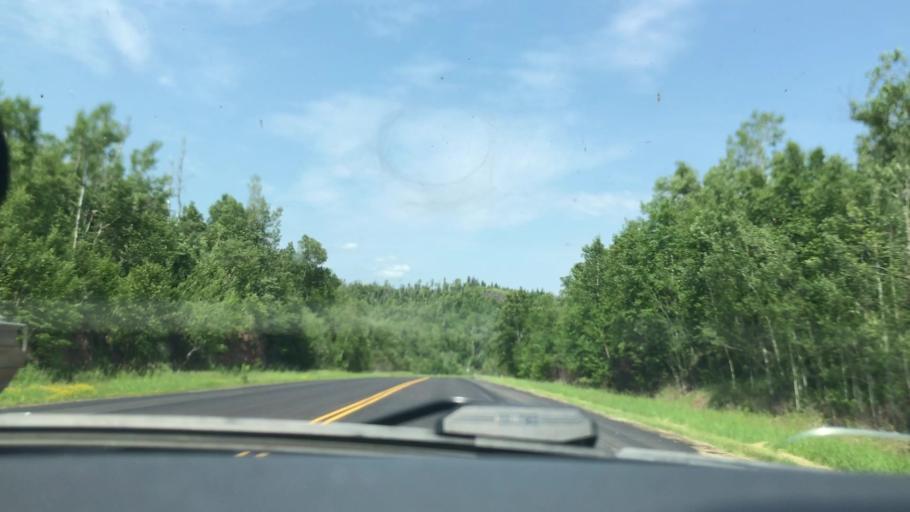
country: US
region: Minnesota
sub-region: Lake County
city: Silver Bay
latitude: 47.3733
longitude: -91.1649
